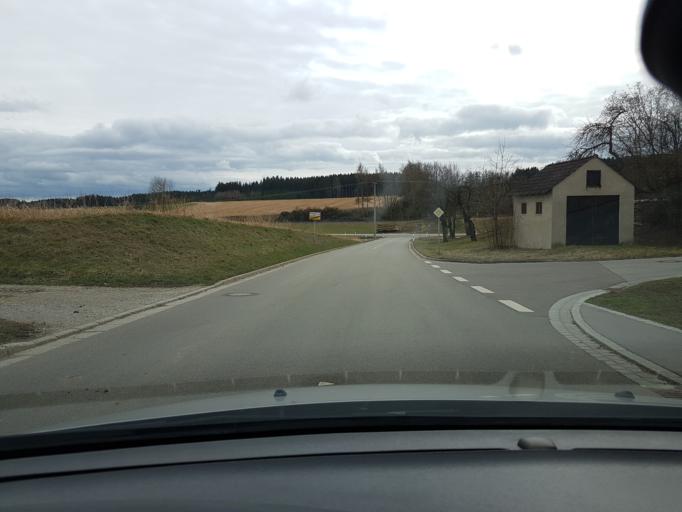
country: DE
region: Bavaria
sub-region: Lower Bavaria
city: Eging
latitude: 48.4923
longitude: 12.2118
